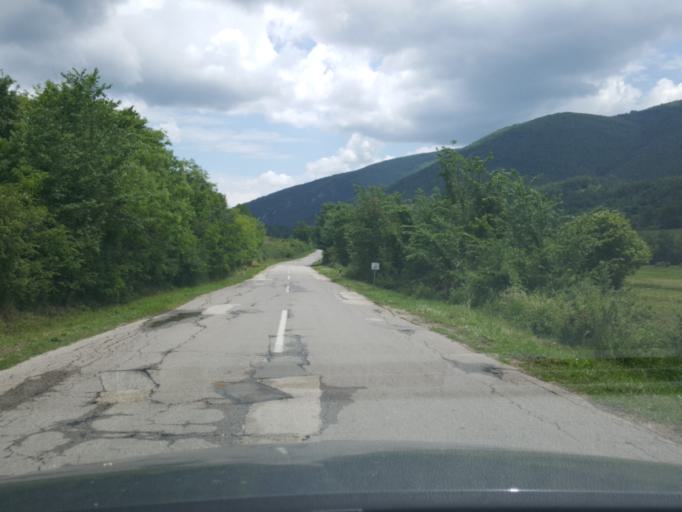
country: RS
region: Central Serbia
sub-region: Zajecarski Okrug
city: Soko Banja
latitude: 43.6389
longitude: 21.9631
